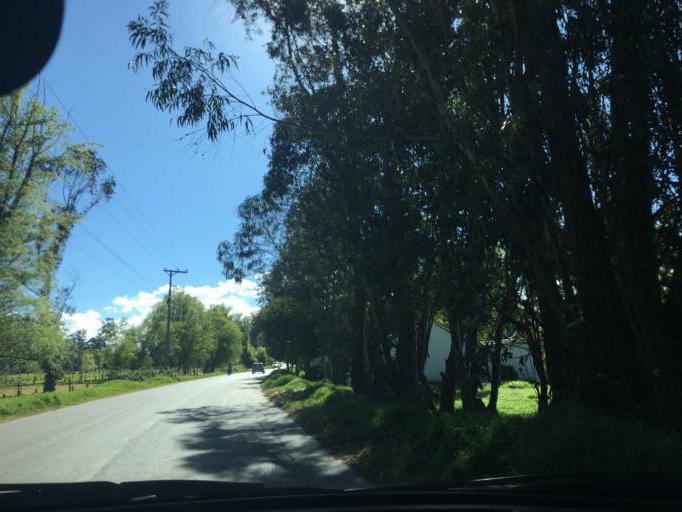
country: CO
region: Boyaca
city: Firavitoba
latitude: 5.6582
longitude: -72.9781
